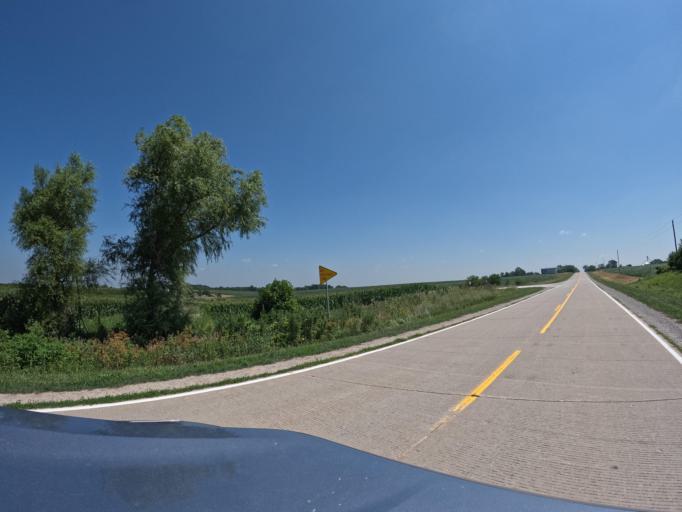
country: US
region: Iowa
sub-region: Keokuk County
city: Sigourney
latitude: 41.2647
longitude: -92.2583
